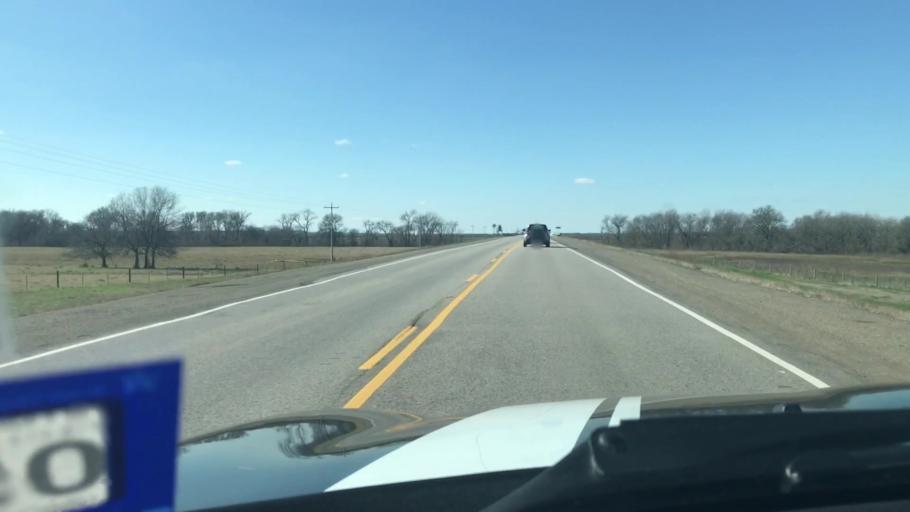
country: US
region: Texas
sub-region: Robertson County
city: Hearne
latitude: 30.8807
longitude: -96.6366
